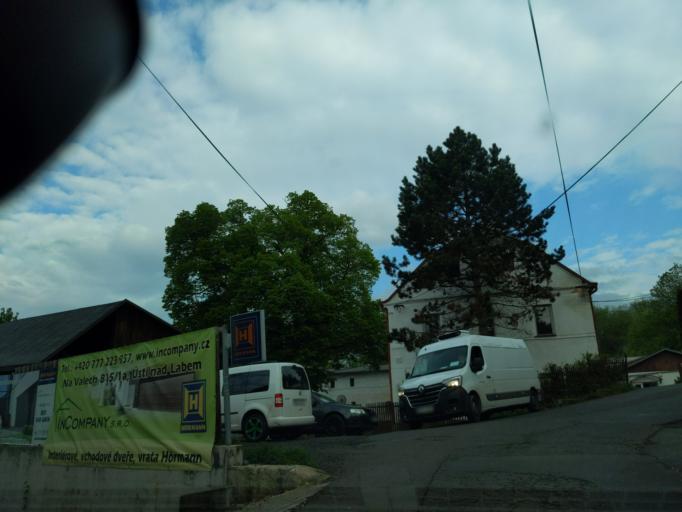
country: CZ
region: Ustecky
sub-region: Okres Usti nad Labem
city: Usti nad Labem
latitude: 50.6816
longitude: 14.0107
